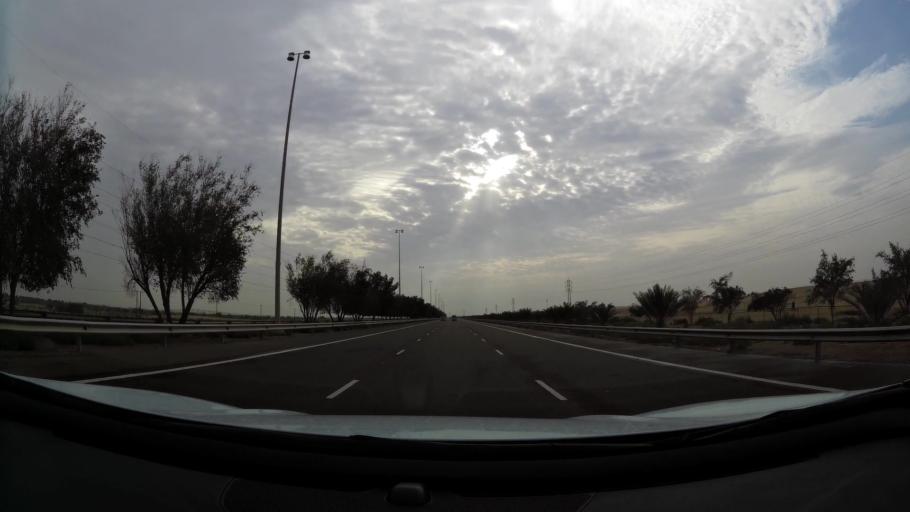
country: AE
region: Abu Dhabi
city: Abu Dhabi
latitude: 24.1978
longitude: 54.9220
